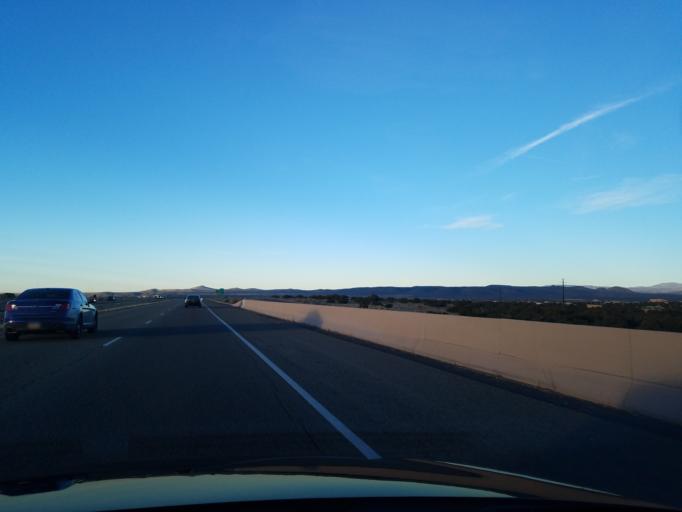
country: US
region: New Mexico
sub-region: Santa Fe County
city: Agua Fria
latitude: 35.6665
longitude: -106.0250
